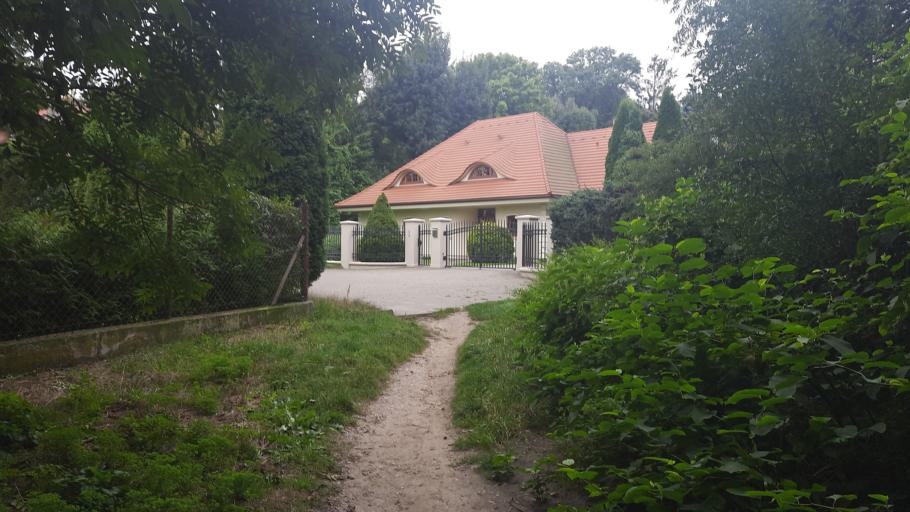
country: PL
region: Lodz Voivodeship
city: Lodz
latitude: 51.8057
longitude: 19.4501
